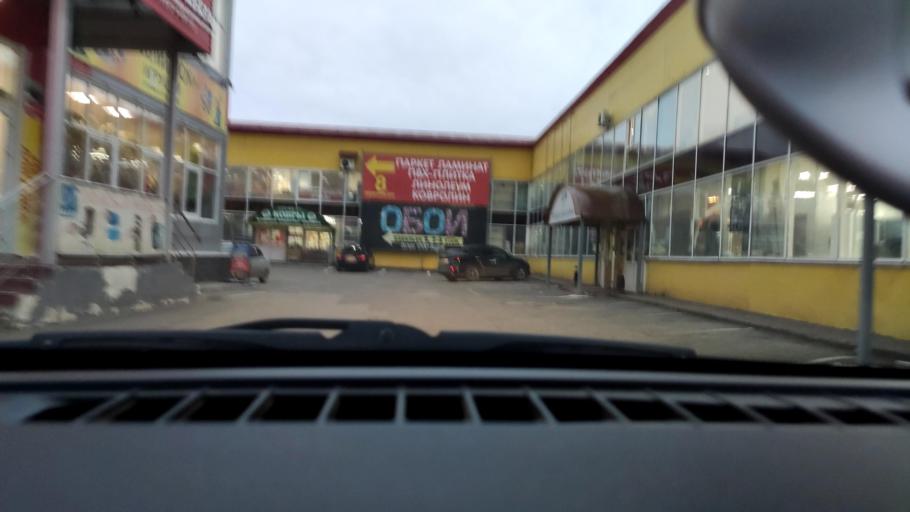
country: RU
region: Perm
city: Kondratovo
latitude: 58.0016
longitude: 56.1447
